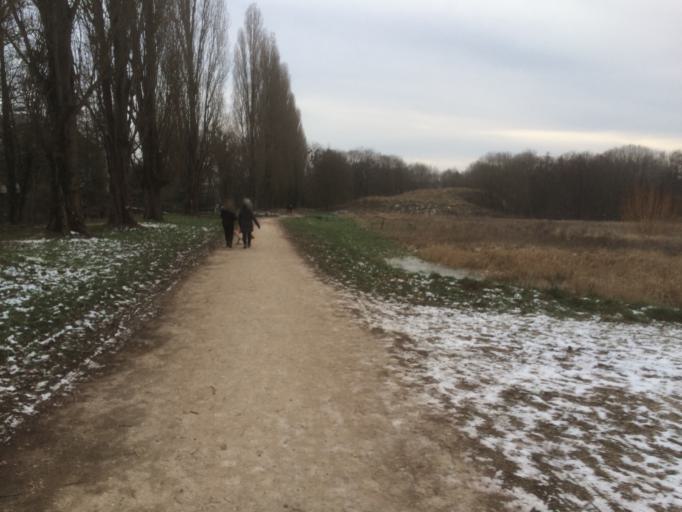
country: FR
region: Ile-de-France
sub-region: Departement de l'Essonne
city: Gif-sur-Yvette
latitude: 48.6991
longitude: 2.1414
